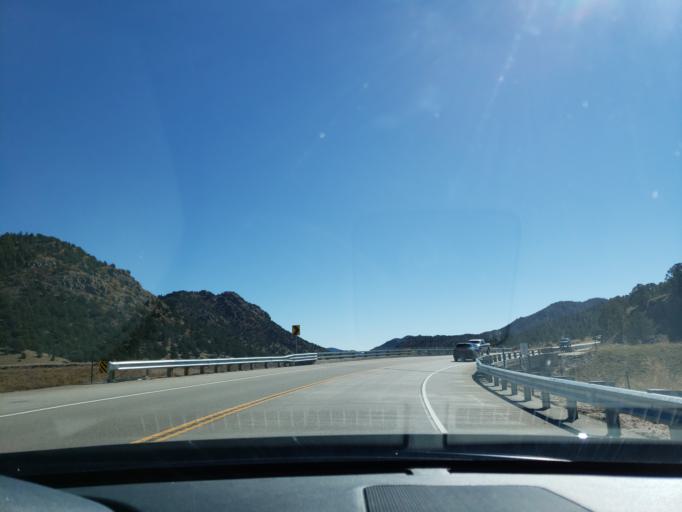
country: US
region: Colorado
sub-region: Fremont County
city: Canon City
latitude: 38.6179
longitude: -105.4454
